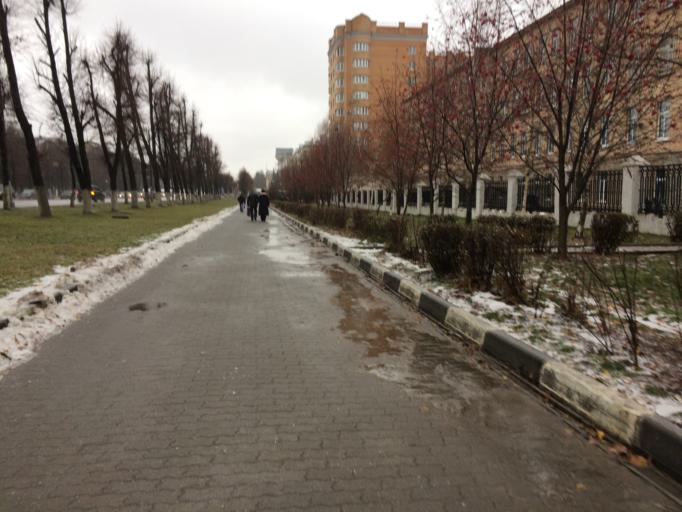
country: RU
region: Tula
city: Mendeleyevskiy
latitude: 54.1701
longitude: 37.5927
